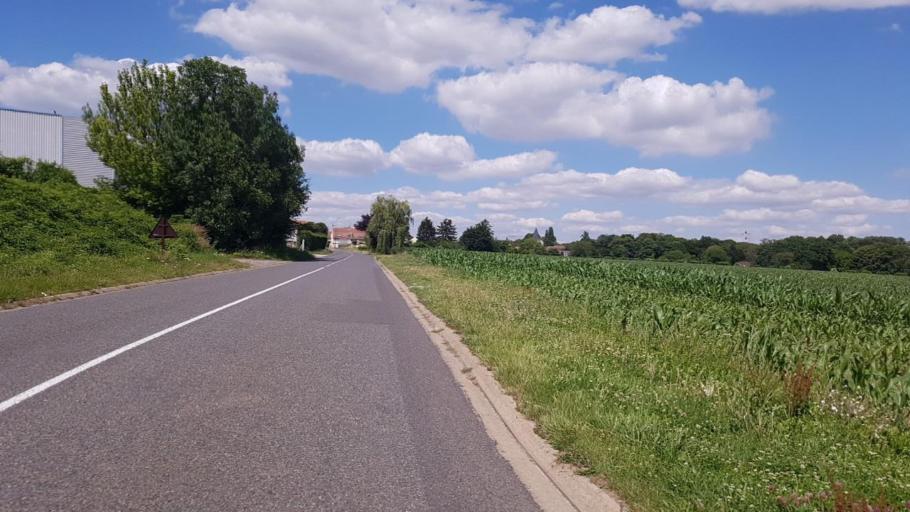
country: FR
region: Ile-de-France
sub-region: Departement de Seine-et-Marne
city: Moussy-le-Vieux
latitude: 49.0306
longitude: 2.6384
